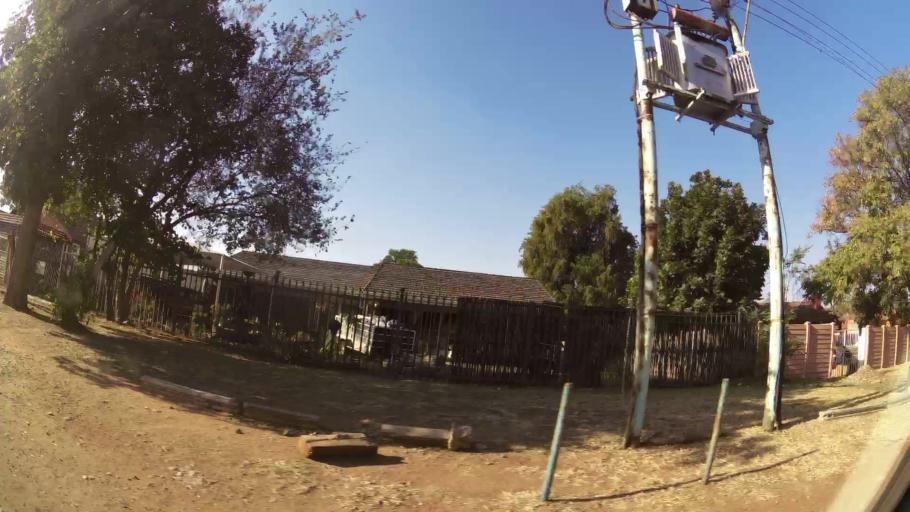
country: ZA
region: North-West
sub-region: Bojanala Platinum District Municipality
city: Rustenburg
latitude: -25.6545
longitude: 27.2586
